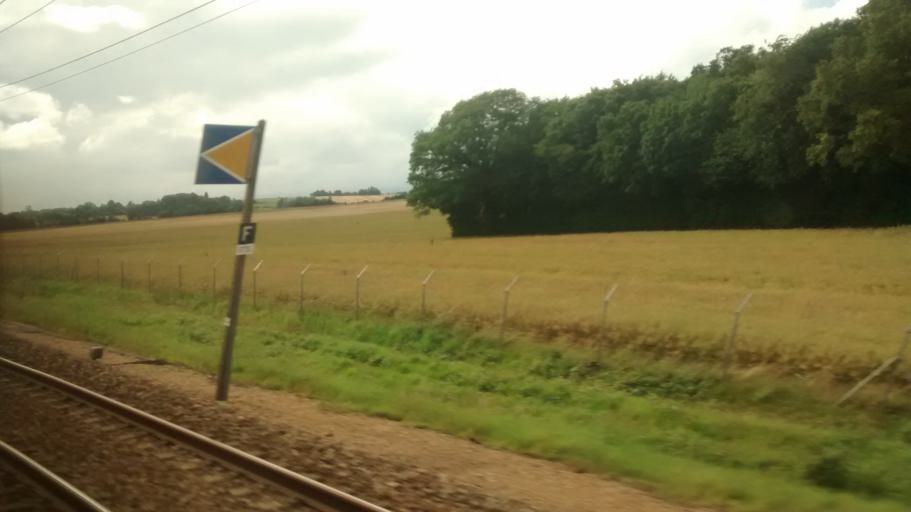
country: FR
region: Centre
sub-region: Departement du Loir-et-Cher
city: Droue
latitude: 48.0705
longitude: 1.0169
